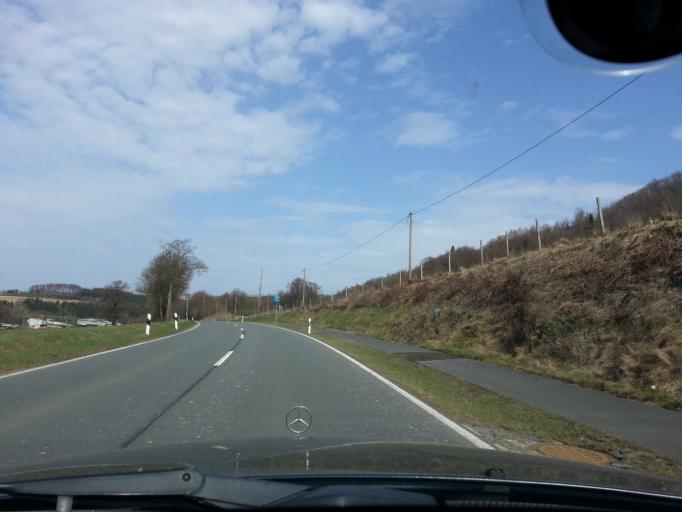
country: DE
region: North Rhine-Westphalia
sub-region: Regierungsbezirk Arnsberg
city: Meschede
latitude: 51.2941
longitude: 8.3263
